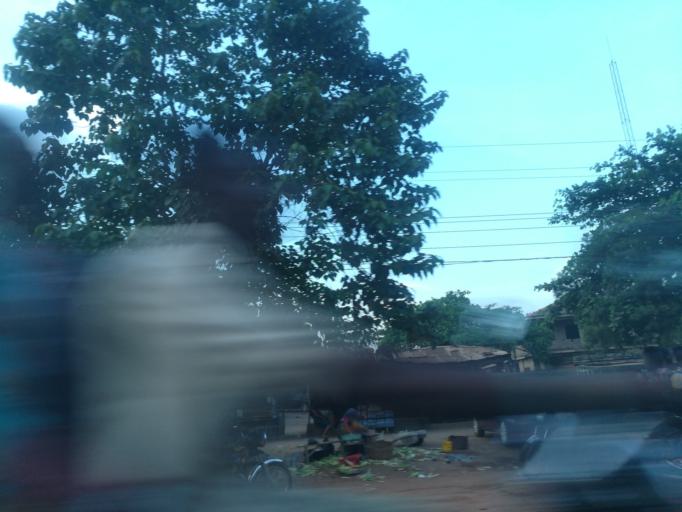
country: NG
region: Ogun
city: Abeokuta
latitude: 7.1767
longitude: 3.3886
